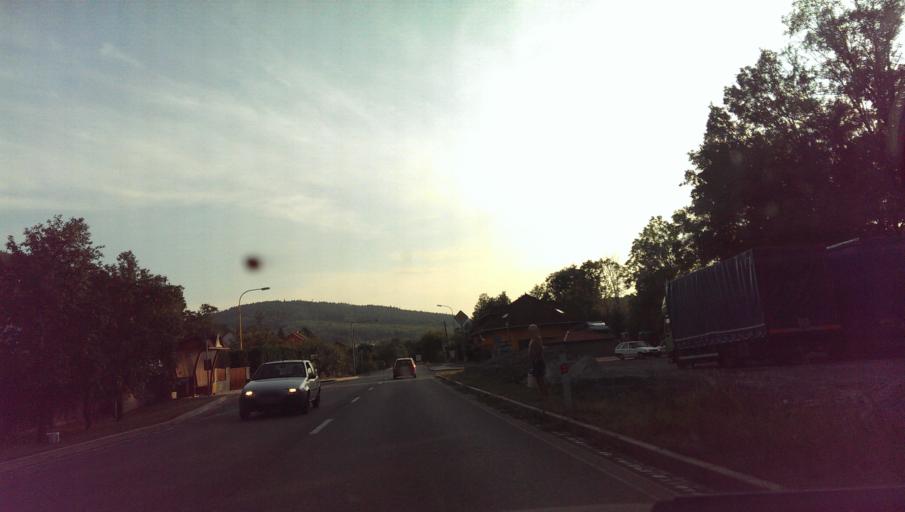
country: CZ
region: Zlin
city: Pozlovice
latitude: 49.1321
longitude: 17.8062
